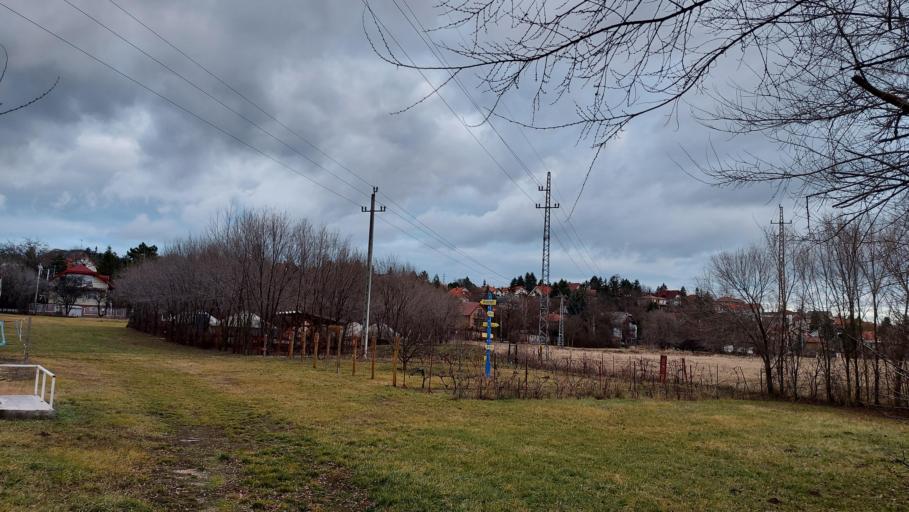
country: HU
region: Pest
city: Toeroekbalint
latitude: 47.4572
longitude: 18.9111
